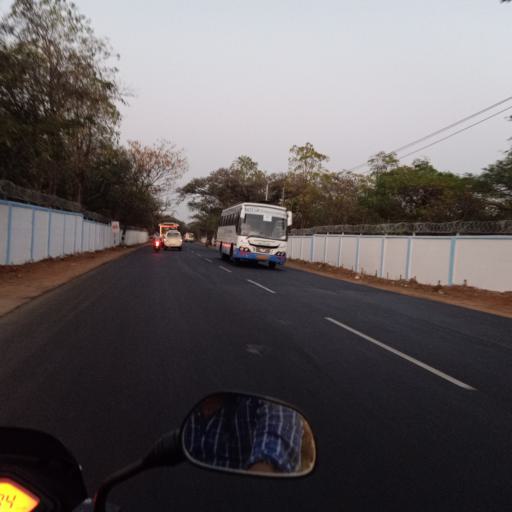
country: IN
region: Telangana
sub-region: Rangareddi
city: Secunderabad
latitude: 17.5558
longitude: 78.5385
